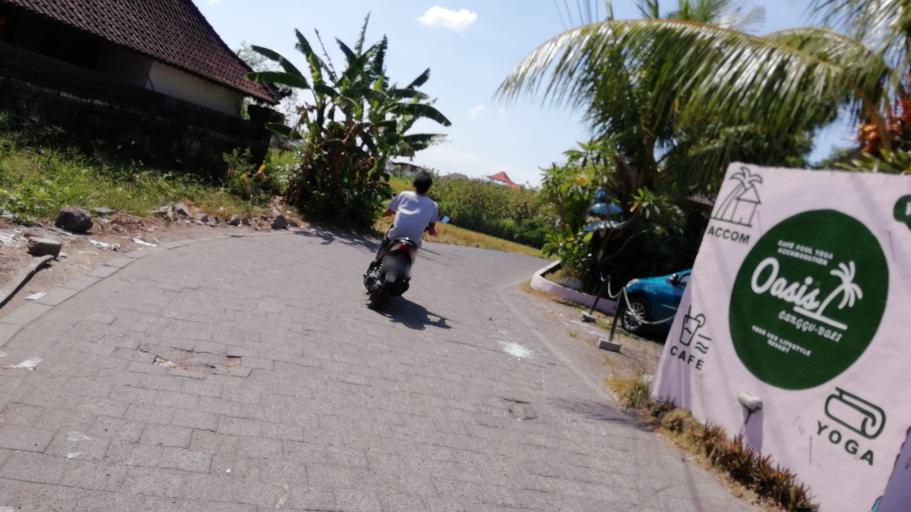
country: ID
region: Bali
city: Banjar Kerobokan
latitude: -8.6532
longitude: 115.1357
